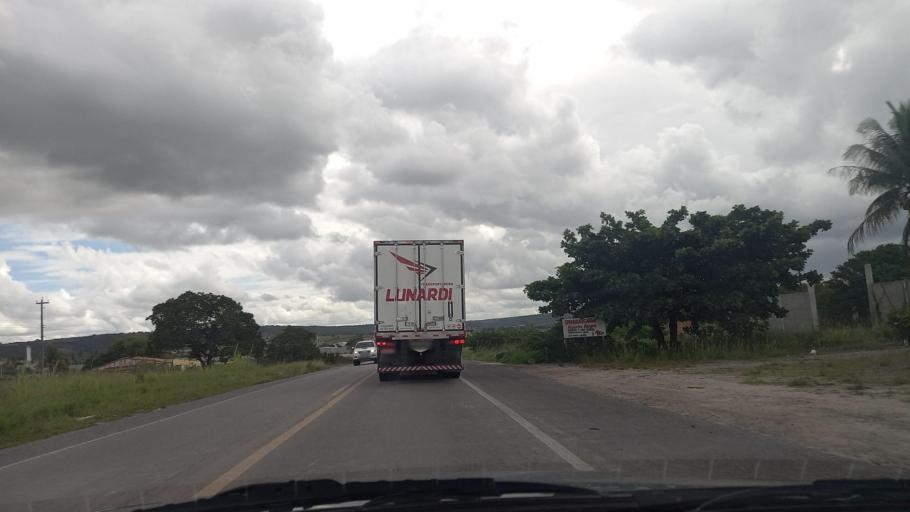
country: BR
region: Pernambuco
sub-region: Lajedo
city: Lajedo
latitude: -8.6622
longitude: -36.3473
